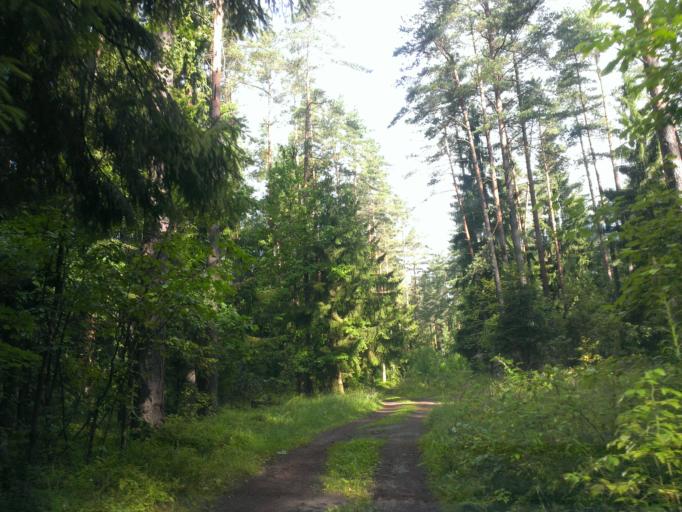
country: LV
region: Incukalns
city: Vangazi
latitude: 57.1005
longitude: 24.5370
